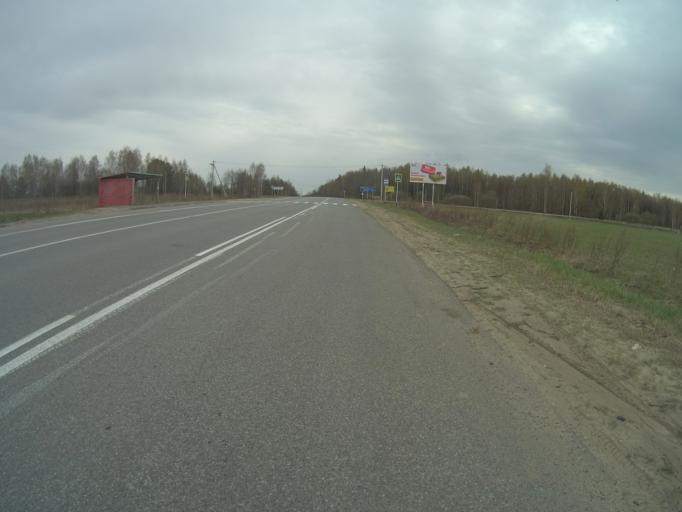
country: RU
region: Vladimir
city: Golovino
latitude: 55.9684
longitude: 40.5502
